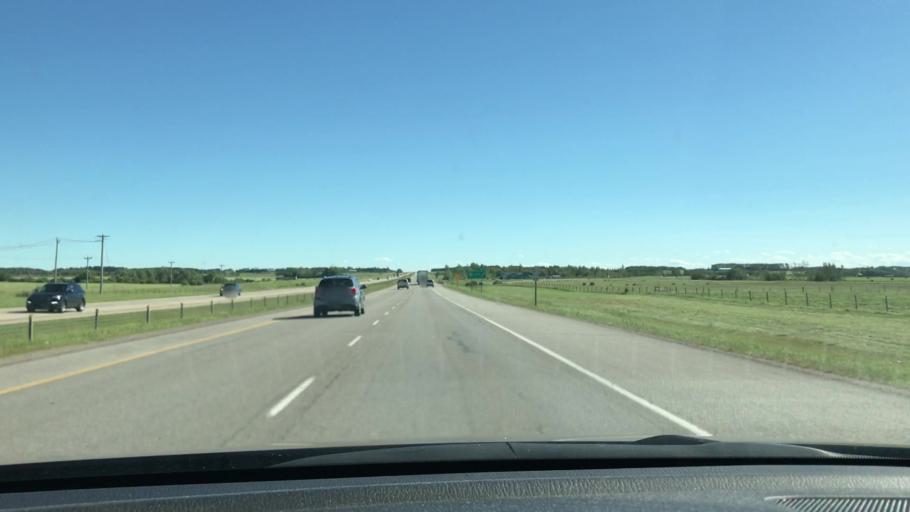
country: CA
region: Alberta
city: Olds
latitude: 51.9127
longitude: -114.0256
